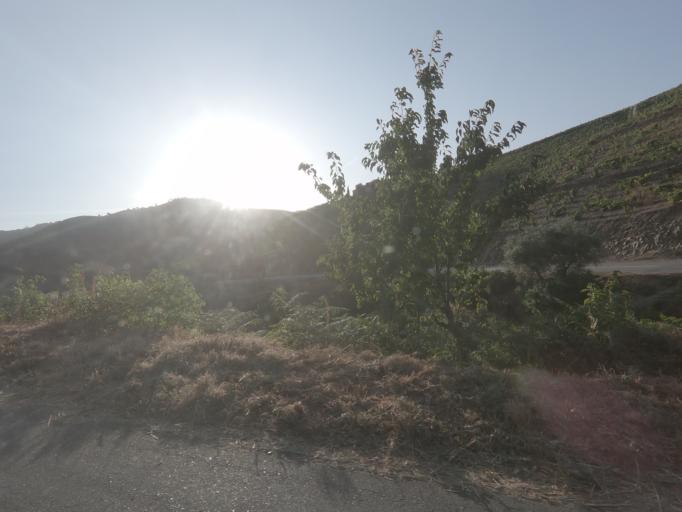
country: PT
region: Vila Real
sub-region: Sabrosa
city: Vilela
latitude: 41.1904
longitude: -7.6355
